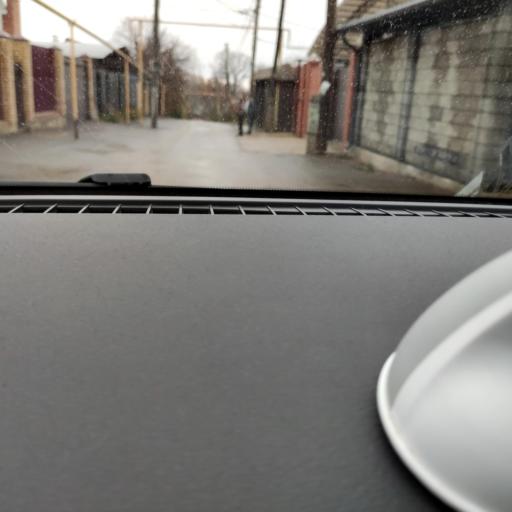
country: RU
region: Samara
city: Samara
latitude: 53.2716
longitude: 50.2106
